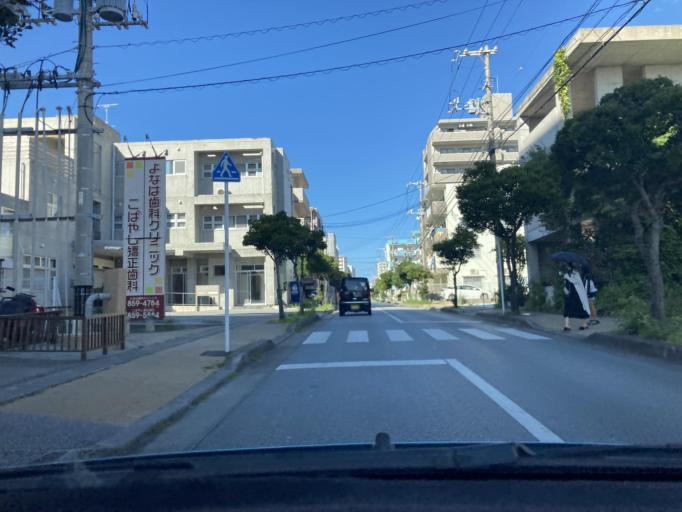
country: JP
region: Okinawa
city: Tomigusuku
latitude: 26.1829
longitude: 127.6565
